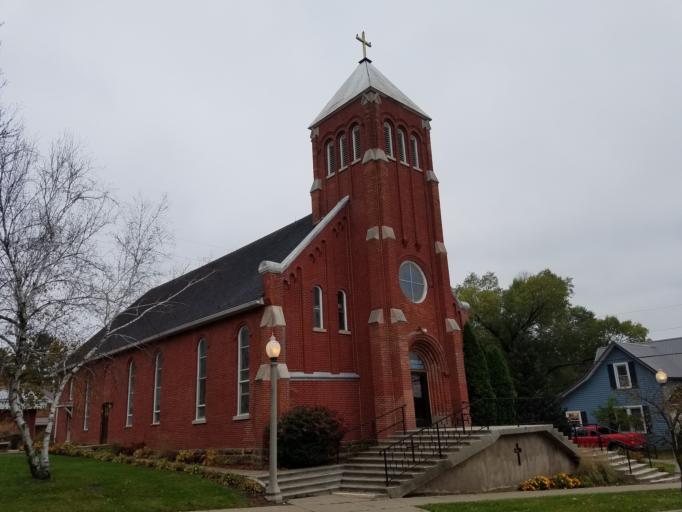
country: US
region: Wisconsin
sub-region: Juneau County
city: Elroy
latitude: 43.6591
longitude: -90.2226
